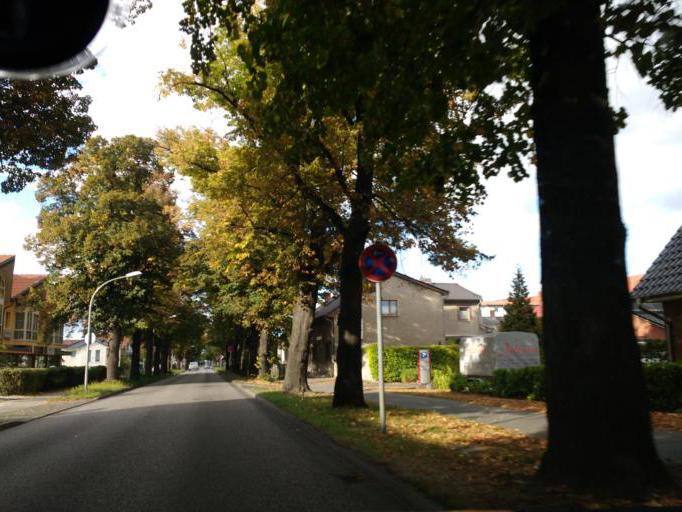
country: DE
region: Berlin
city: Lichtenrade
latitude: 52.3991
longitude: 13.4418
